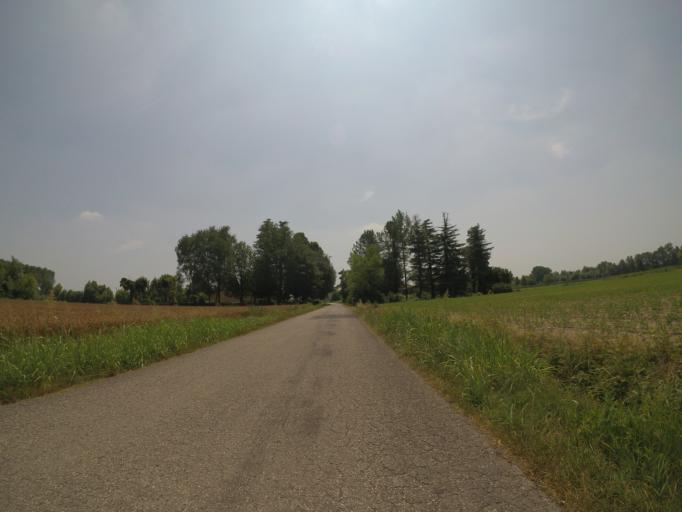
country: IT
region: Friuli Venezia Giulia
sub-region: Provincia di Udine
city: Rivignano
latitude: 45.8772
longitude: 13.0519
